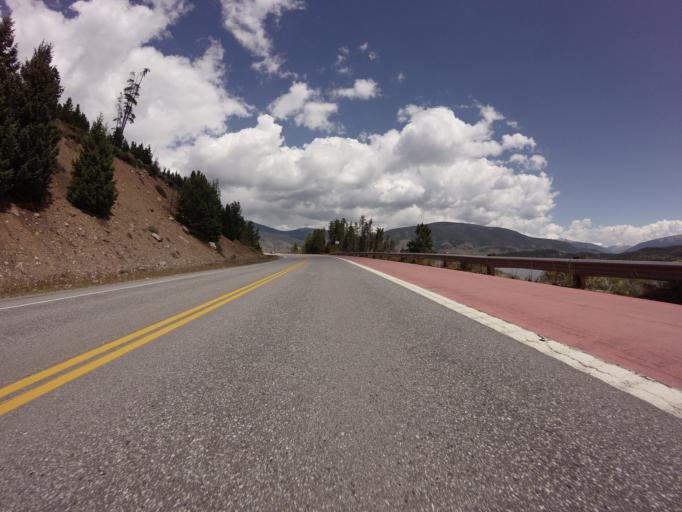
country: US
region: Colorado
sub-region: Summit County
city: Silverthorne
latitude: 39.6123
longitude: -106.0657
